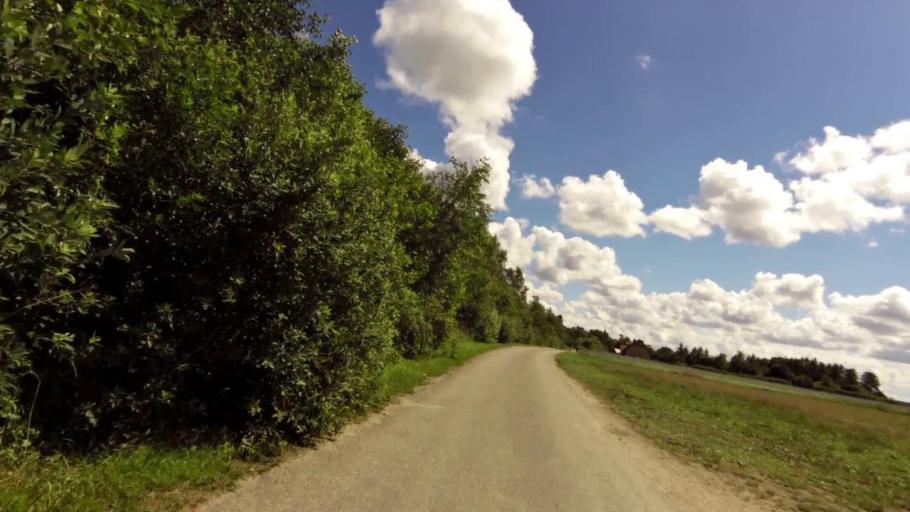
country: PL
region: West Pomeranian Voivodeship
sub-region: Powiat slawienski
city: Slawno
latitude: 54.5265
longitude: 16.6072
